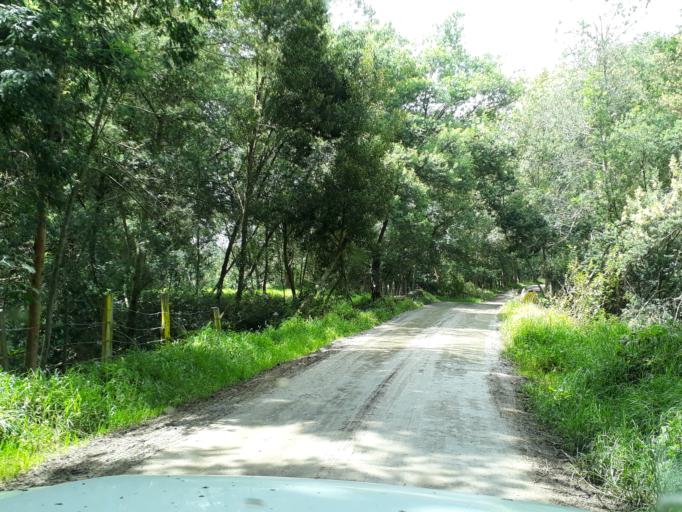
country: CO
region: Cundinamarca
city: Guasca
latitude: 4.8901
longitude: -73.8862
